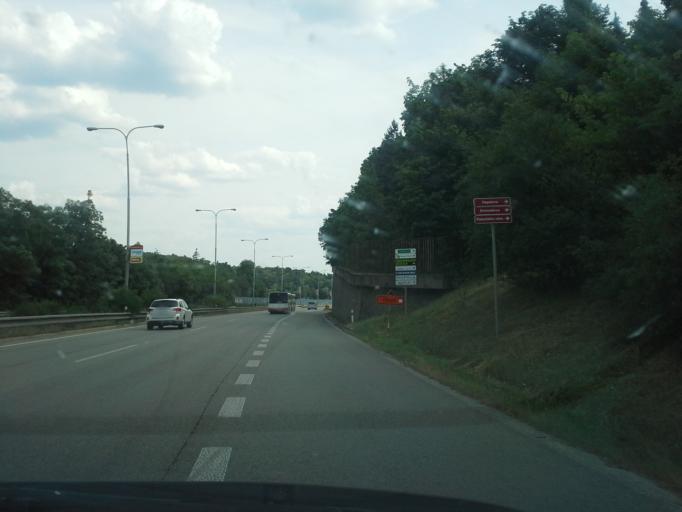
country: CZ
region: South Moravian
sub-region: Mesto Brno
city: Mokra Hora
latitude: 49.2536
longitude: 16.5871
